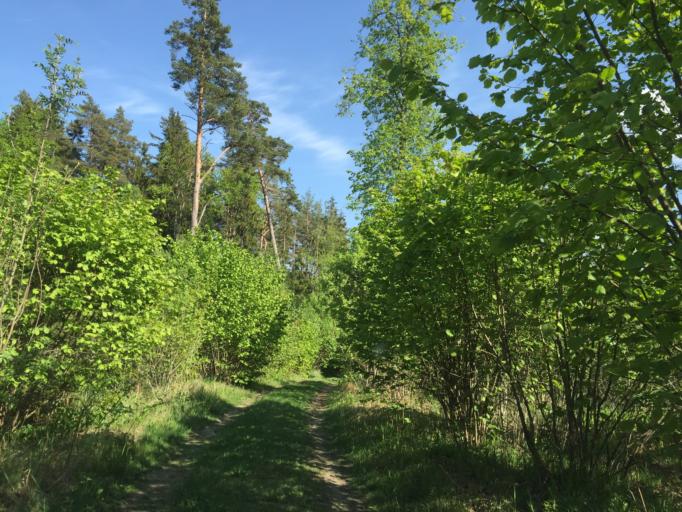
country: LV
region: Baldone
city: Baldone
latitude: 56.7967
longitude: 24.3774
